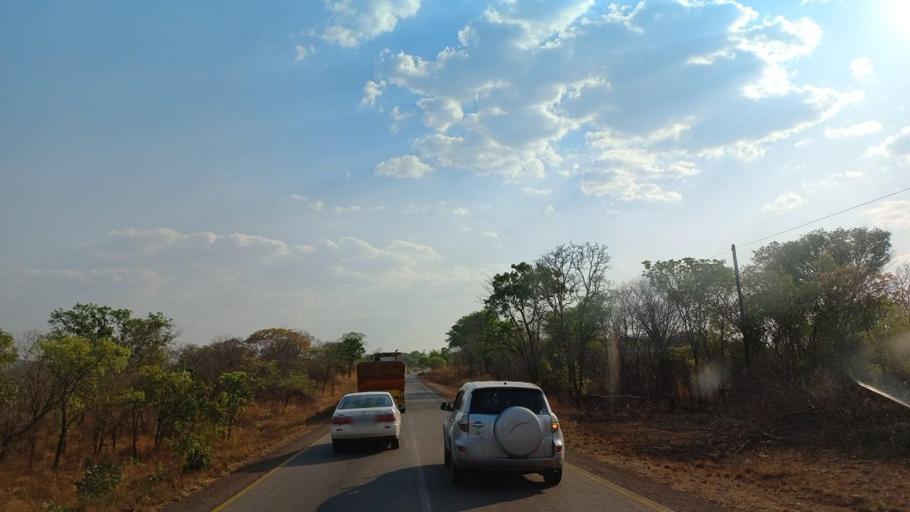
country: ZM
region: Lusaka
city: Luangwa
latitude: -14.9822
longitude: 29.9895
